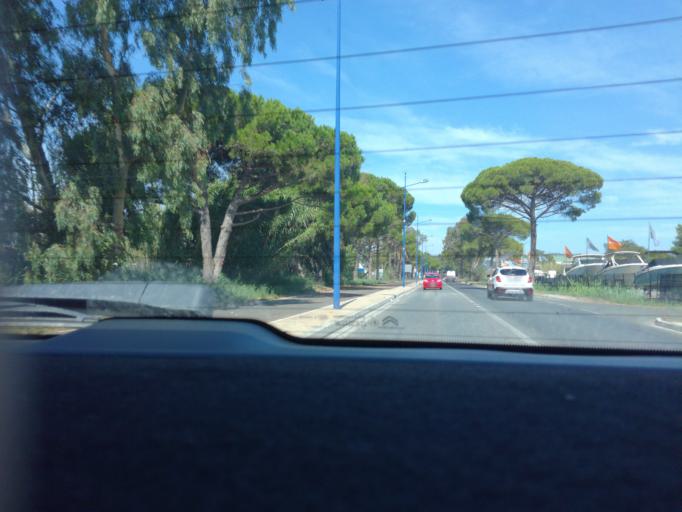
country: FR
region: Provence-Alpes-Cote d'Azur
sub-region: Departement du Var
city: Hyeres
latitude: 43.0857
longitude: 6.1474
